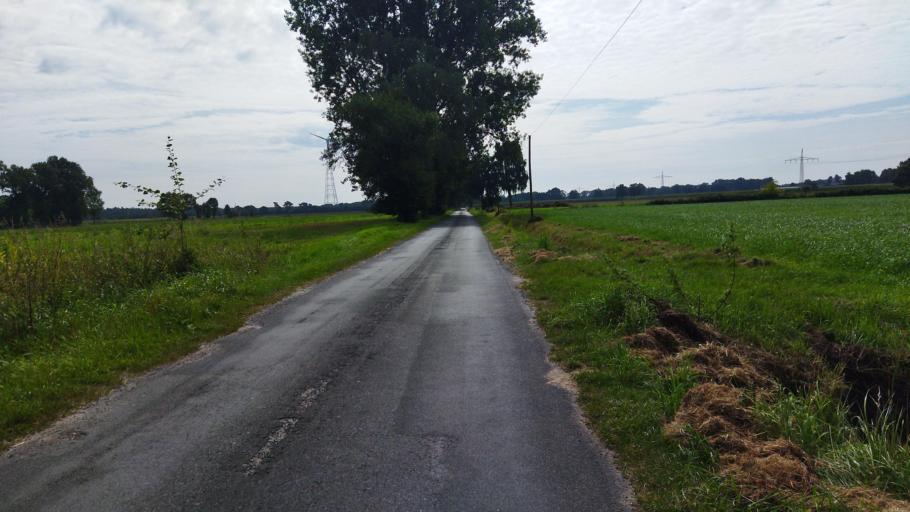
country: DE
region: North Rhine-Westphalia
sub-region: Regierungsbezirk Munster
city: Lienen
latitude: 52.1218
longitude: 7.9982
